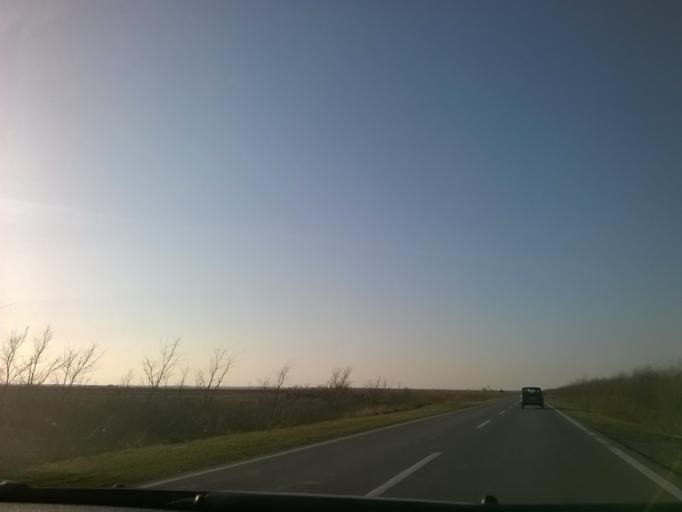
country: RS
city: Uljma
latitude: 45.0491
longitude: 21.1126
